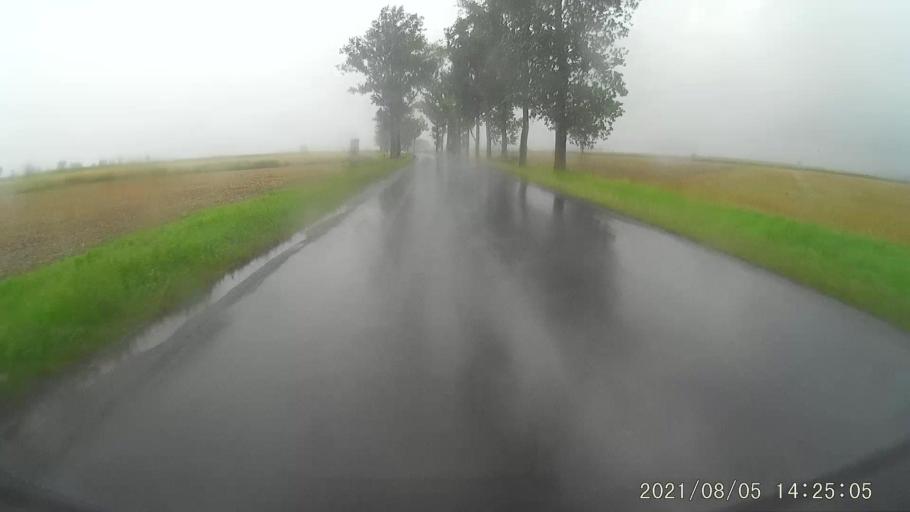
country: PL
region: Opole Voivodeship
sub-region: Powiat nyski
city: Korfantow
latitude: 50.4827
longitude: 17.6224
